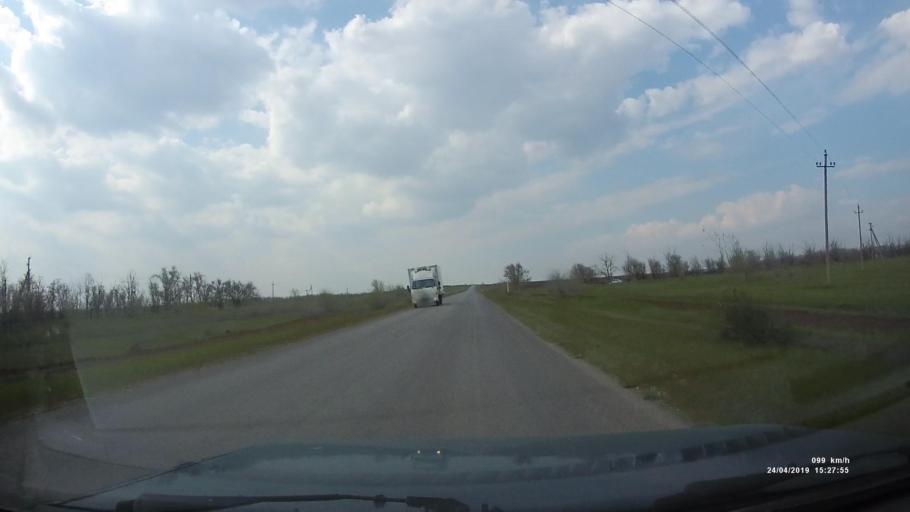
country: RU
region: Rostov
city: Remontnoye
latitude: 46.5715
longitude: 43.0223
